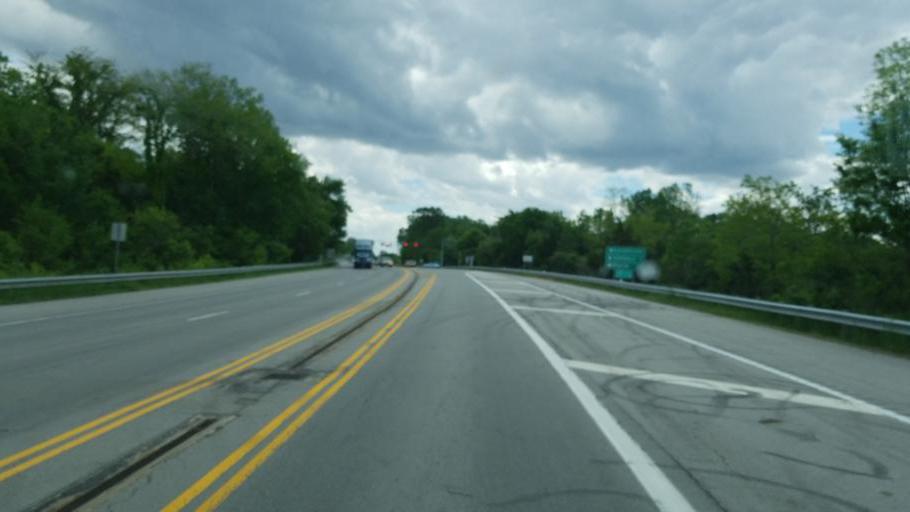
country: US
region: Ohio
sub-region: Erie County
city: Milan
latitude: 41.2977
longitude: -82.6101
